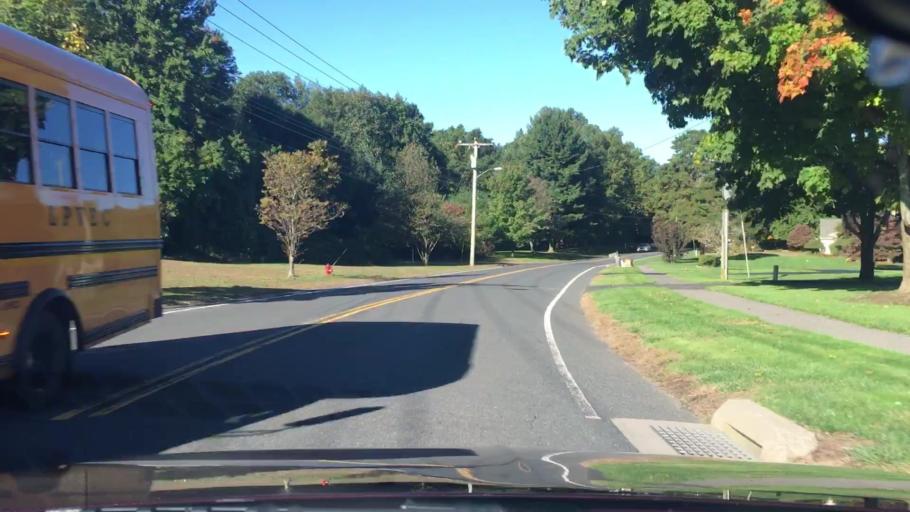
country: US
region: Connecticut
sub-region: Hartford County
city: Sherwood Manor
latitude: 42.0380
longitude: -72.5386
